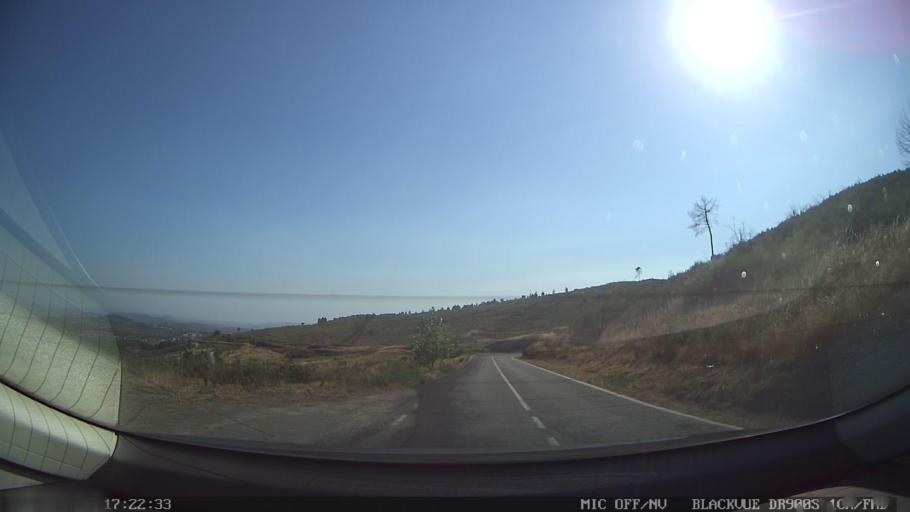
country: PT
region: Vila Real
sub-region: Murca
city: Murca
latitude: 41.3049
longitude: -7.4749
